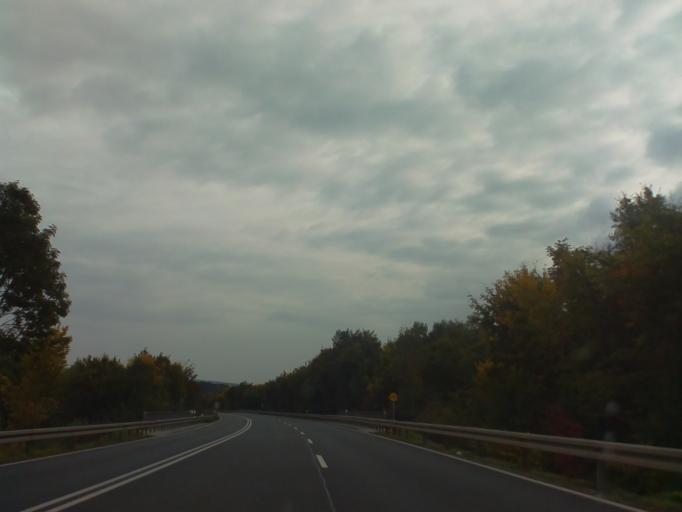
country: DE
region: Hesse
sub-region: Regierungsbezirk Kassel
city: Hunfeld
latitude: 50.6824
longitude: 9.7529
